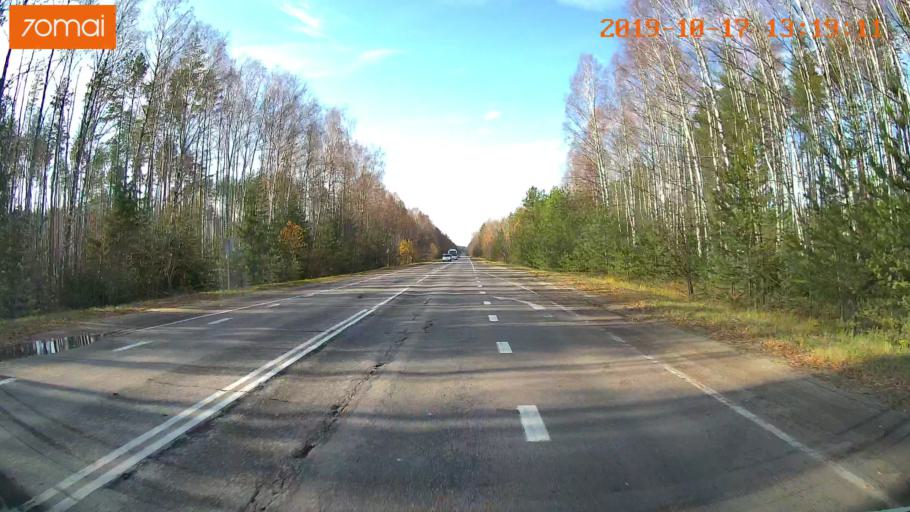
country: RU
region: Rjazan
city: Gus'-Zheleznyy
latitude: 55.0678
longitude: 41.0801
